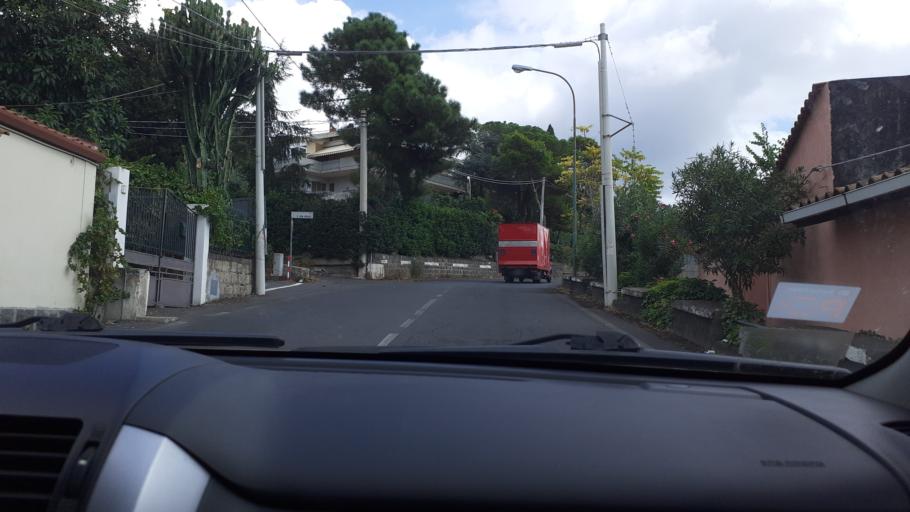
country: IT
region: Sicily
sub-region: Catania
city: Carrubazza-Motta
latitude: 37.5515
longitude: 15.1027
